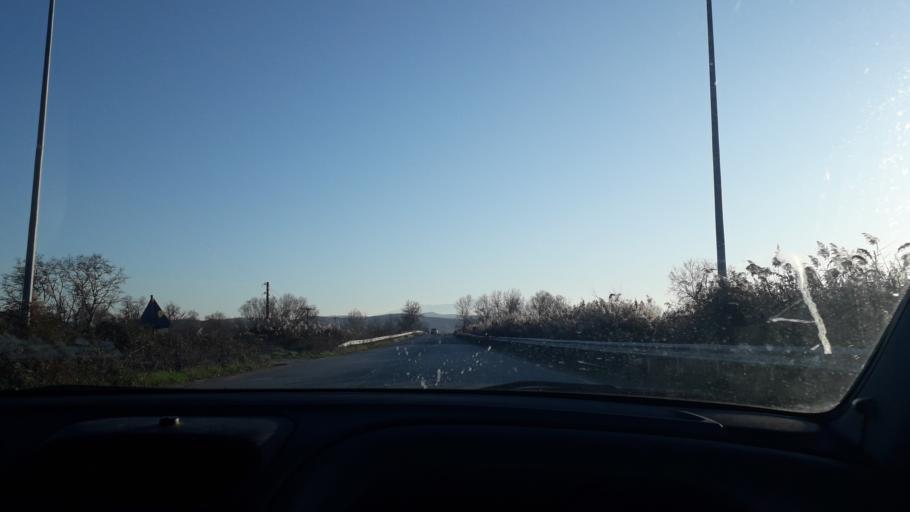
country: GR
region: Central Macedonia
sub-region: Nomos Imathias
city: Agkathia
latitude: 40.5849
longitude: 22.4714
